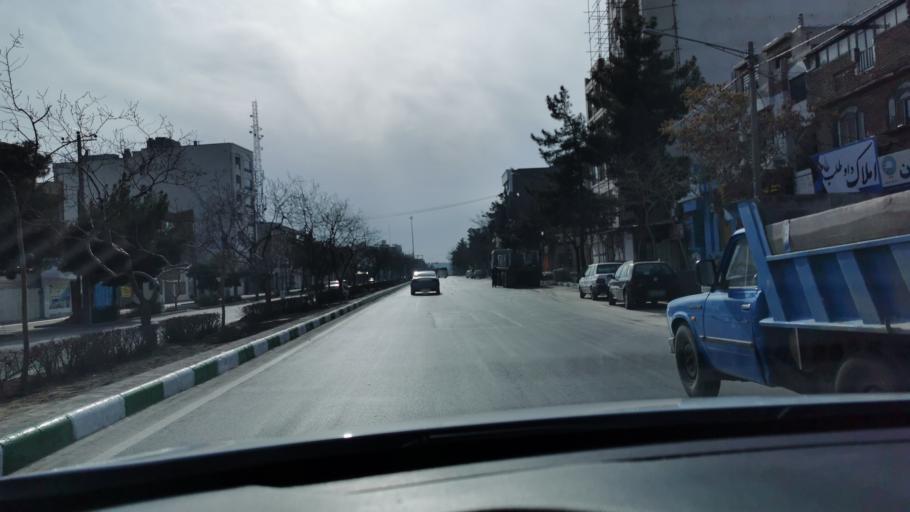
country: IR
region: Razavi Khorasan
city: Mashhad
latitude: 36.2923
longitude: 59.5352
